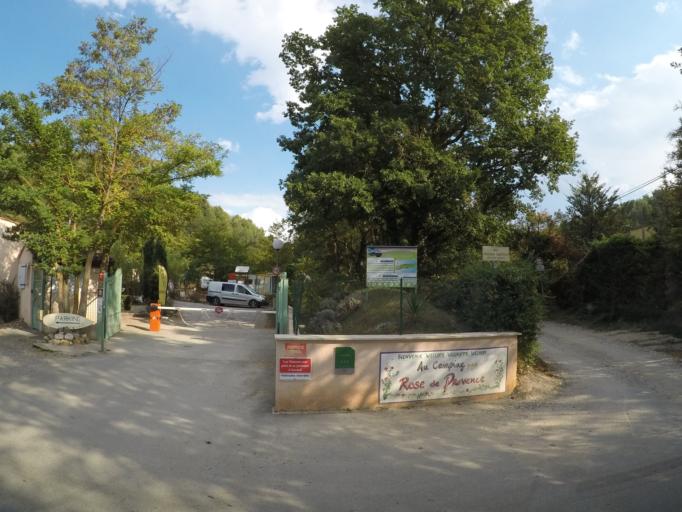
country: FR
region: Provence-Alpes-Cote d'Azur
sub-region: Departement des Alpes-de-Haute-Provence
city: Riez
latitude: 43.8131
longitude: 6.0988
